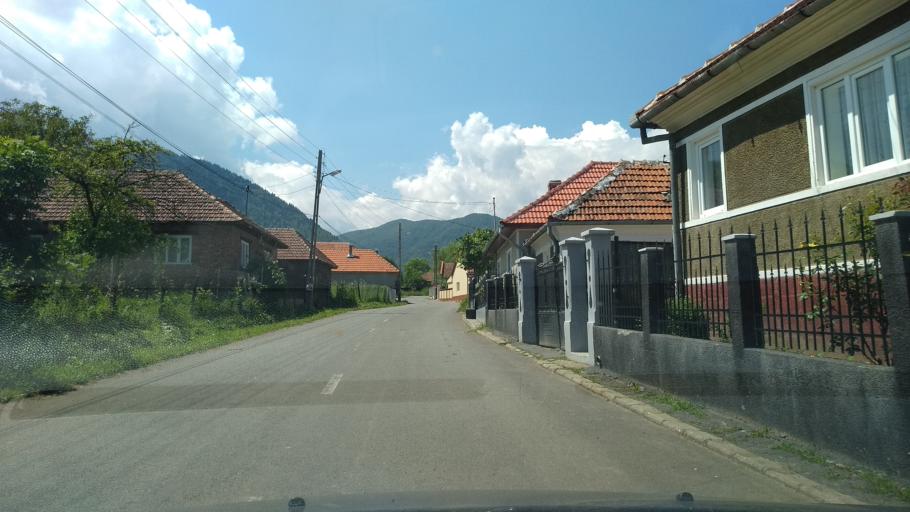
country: RO
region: Hunedoara
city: Salasu de Sus
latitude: 45.4846
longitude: 22.9240
